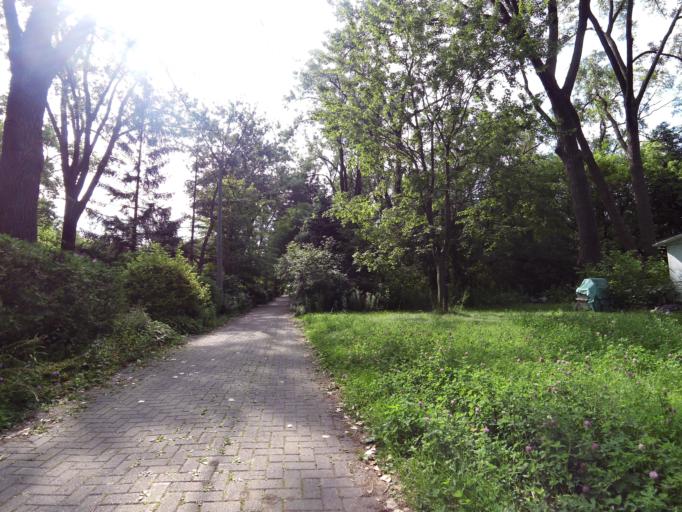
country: CA
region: Ontario
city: Toronto
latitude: 43.6283
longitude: -79.3605
